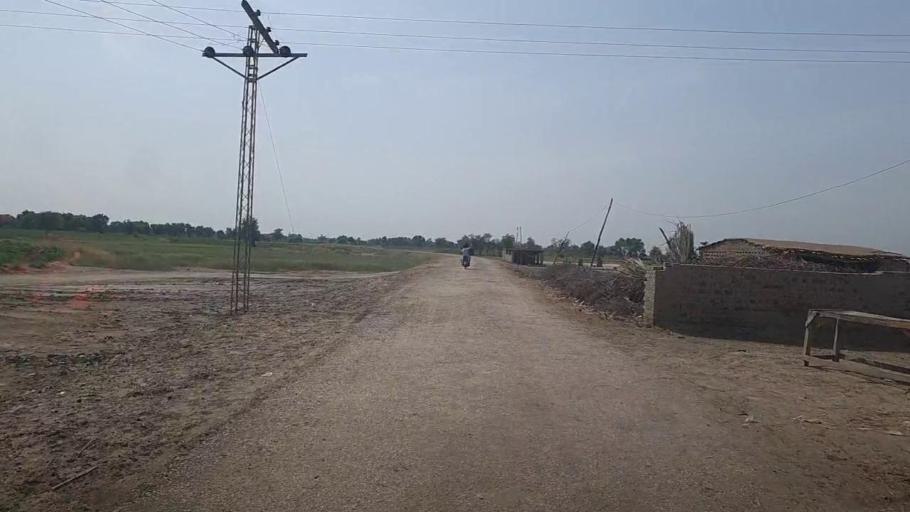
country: PK
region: Sindh
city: Ubauro
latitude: 28.1373
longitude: 69.8237
